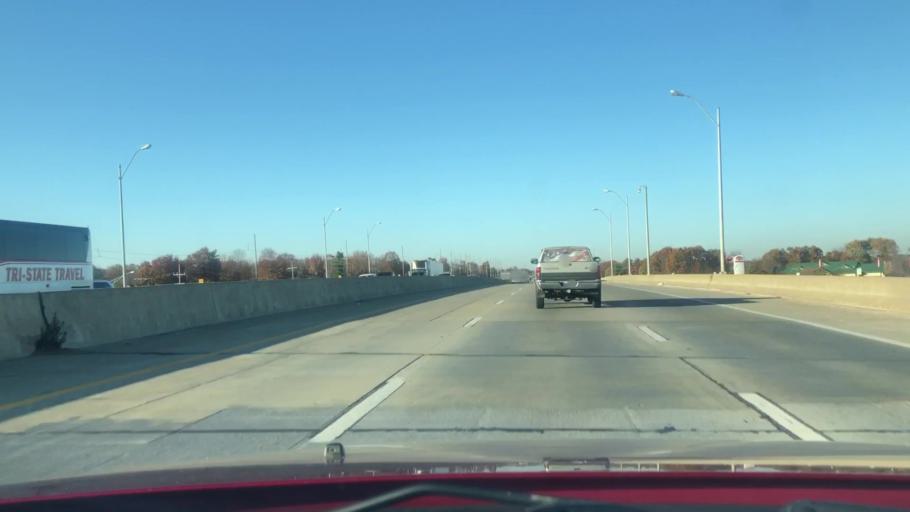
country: US
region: Missouri
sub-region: Greene County
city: Springfield
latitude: 37.1798
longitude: -93.2245
